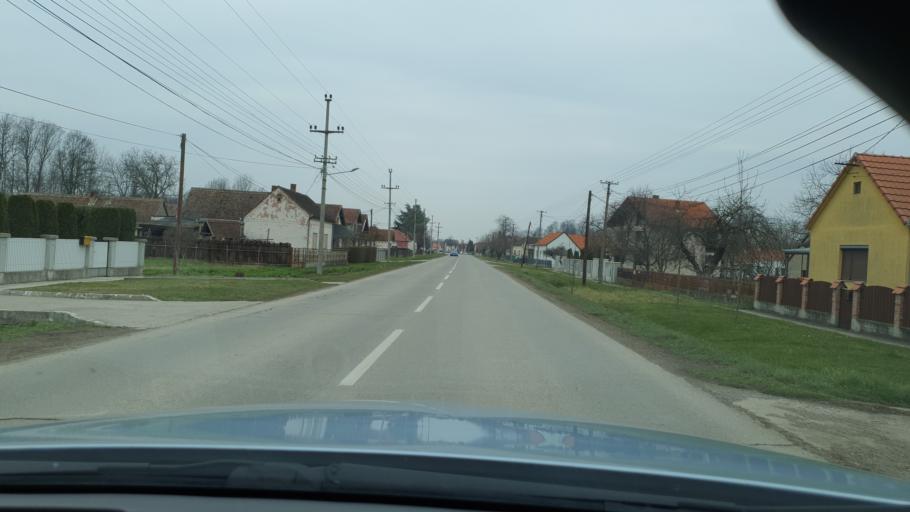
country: RS
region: Central Serbia
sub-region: Macvanski Okrug
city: Bogatic
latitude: 44.8332
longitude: 19.4972
